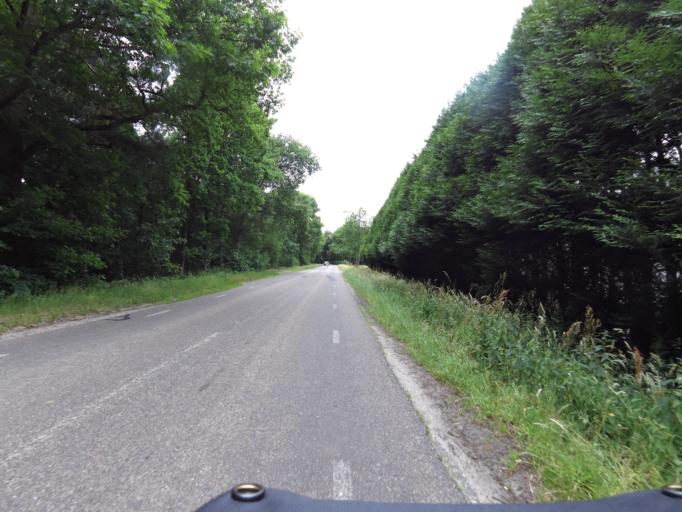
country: NL
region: North Brabant
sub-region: Gemeente Oirschot
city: Middelbeers
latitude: 51.4409
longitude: 5.2125
